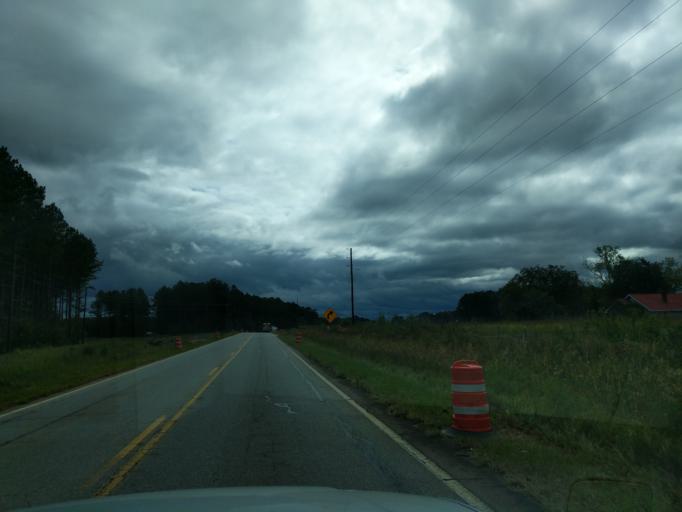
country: US
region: Georgia
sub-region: Wilkes County
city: Washington
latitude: 33.6859
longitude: -82.6465
